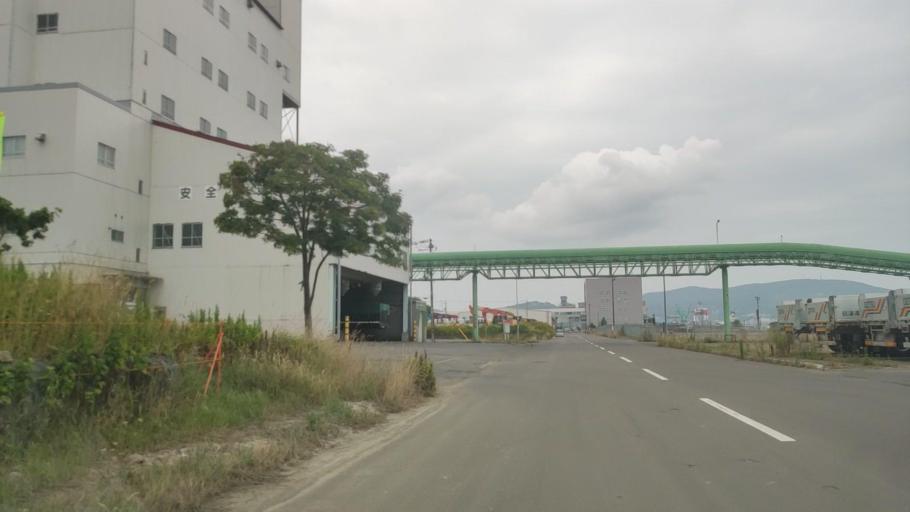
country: JP
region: Hokkaido
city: Otaru
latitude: 43.1884
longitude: 141.0223
